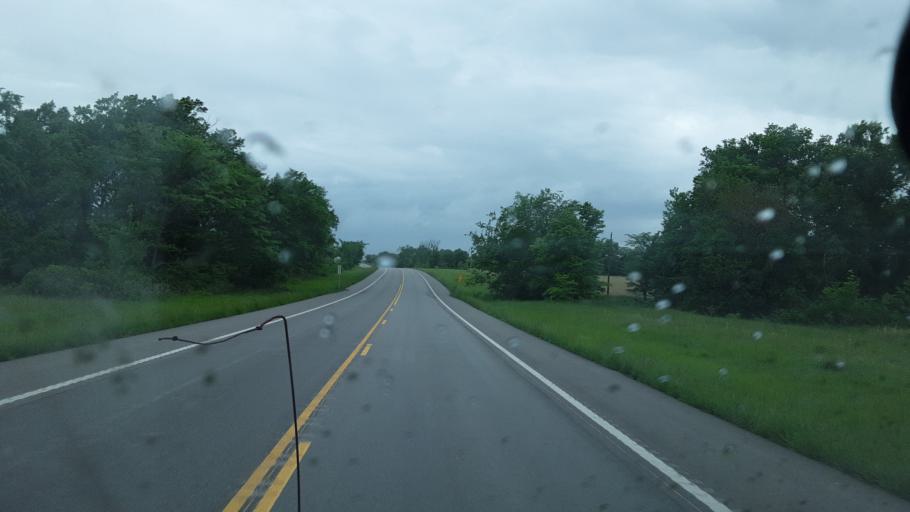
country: US
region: Missouri
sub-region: Marion County
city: Monroe City
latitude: 39.5865
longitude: -91.8006
